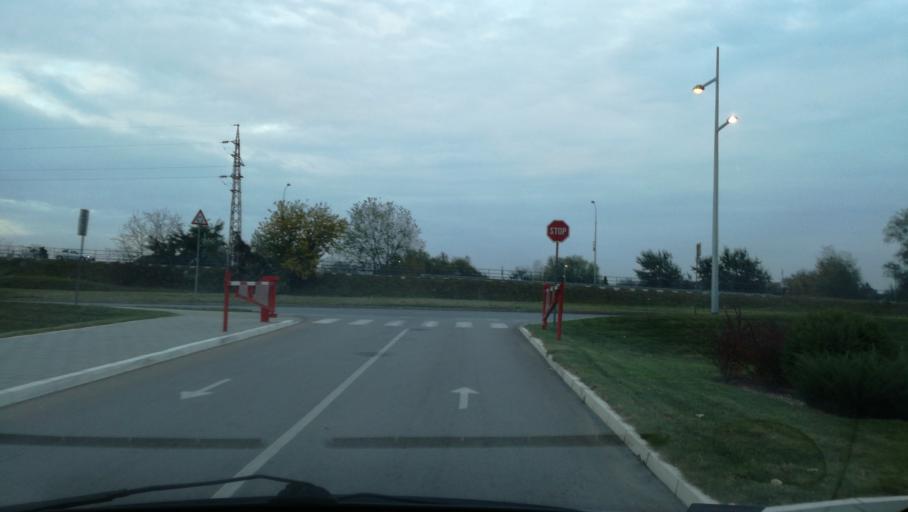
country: RS
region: Autonomna Pokrajina Vojvodina
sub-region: Juznobacki Okrug
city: Novi Sad
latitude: 45.2767
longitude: 19.8279
